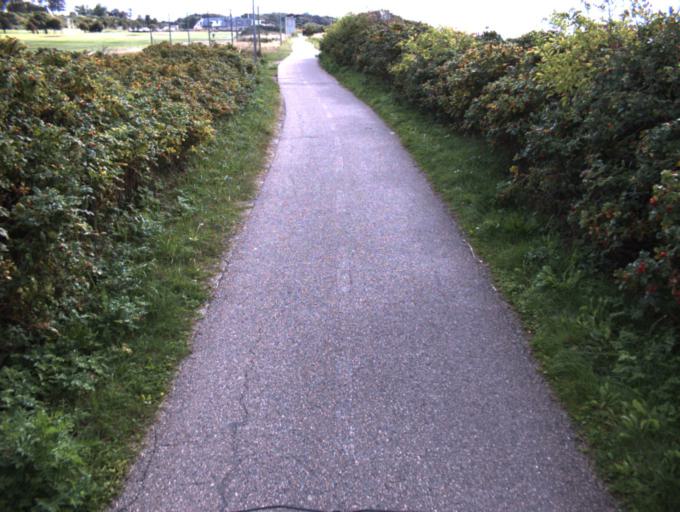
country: SE
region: Skane
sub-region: Helsingborg
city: Rydeback
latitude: 55.9793
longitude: 12.7547
